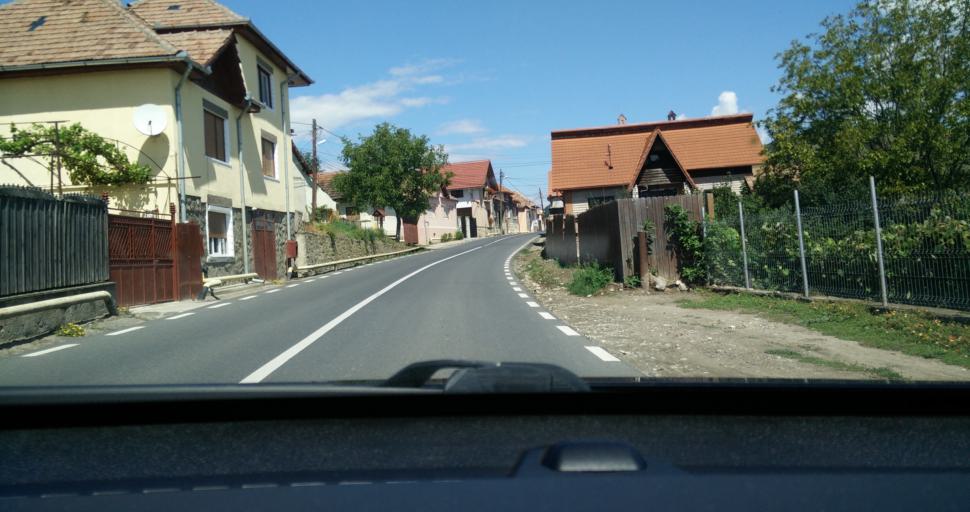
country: RO
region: Alba
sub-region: Comuna Sasciori
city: Sebesel
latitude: 45.8839
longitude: 23.5657
